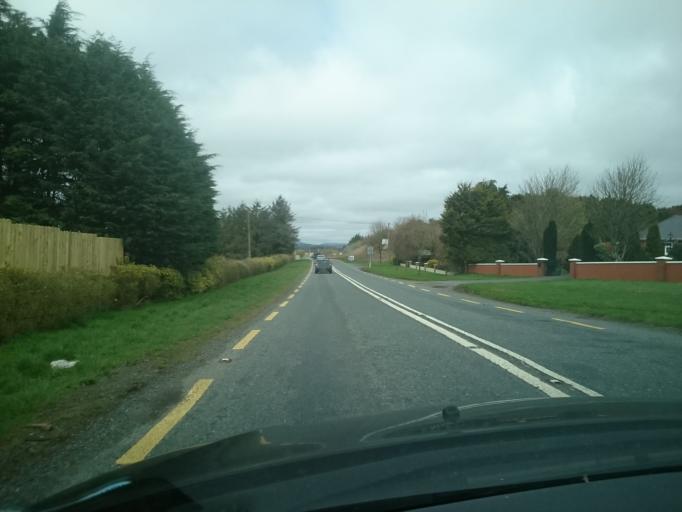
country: IE
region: Connaught
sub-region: Maigh Eo
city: Castlebar
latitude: 53.8332
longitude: -9.1852
